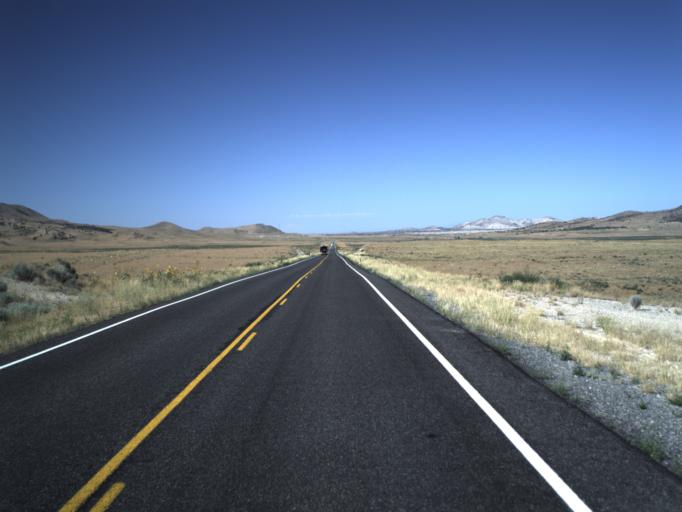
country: US
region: Utah
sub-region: Juab County
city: Mona
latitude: 39.6974
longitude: -112.2252
